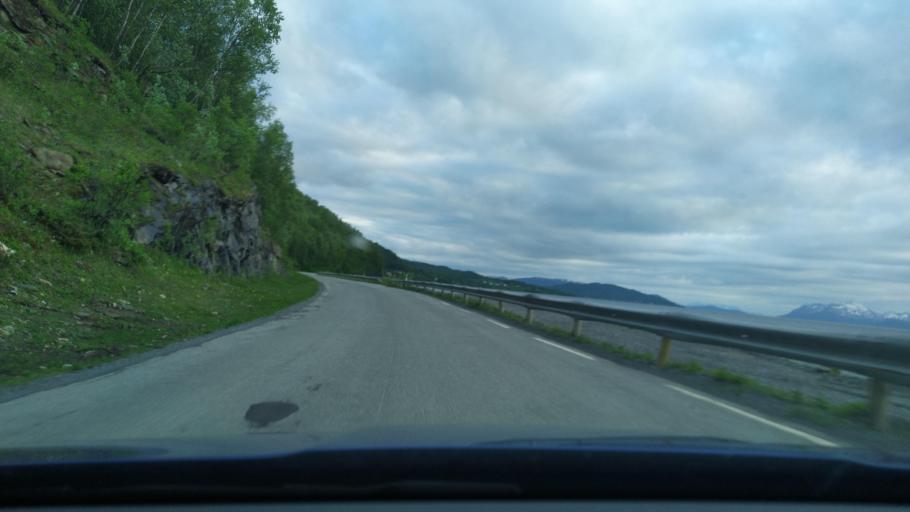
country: NO
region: Troms
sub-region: Lenvik
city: Finnsnes
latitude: 69.1449
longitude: 17.9248
